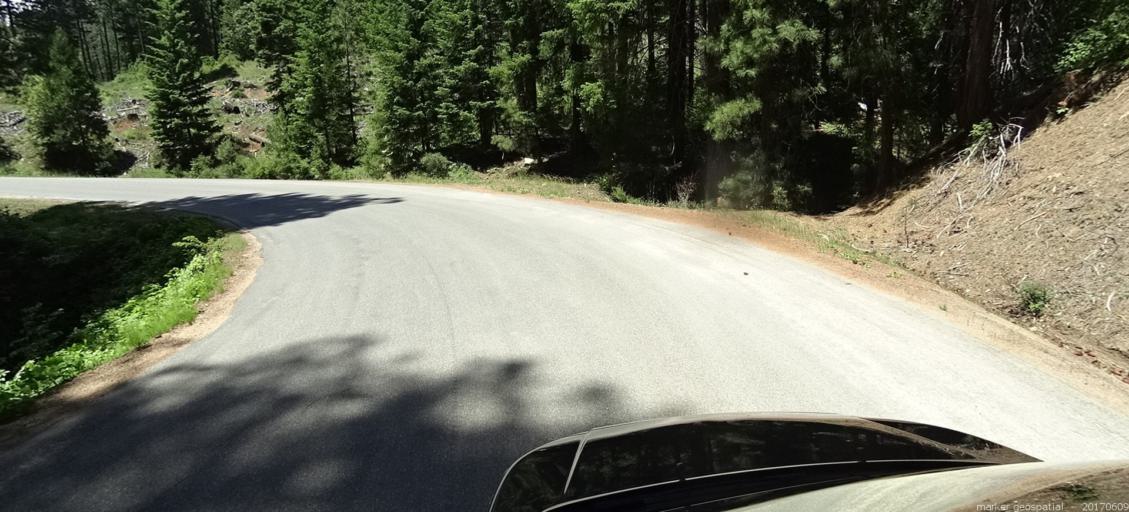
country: US
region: California
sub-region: Siskiyou County
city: Yreka
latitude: 41.4295
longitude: -122.9426
